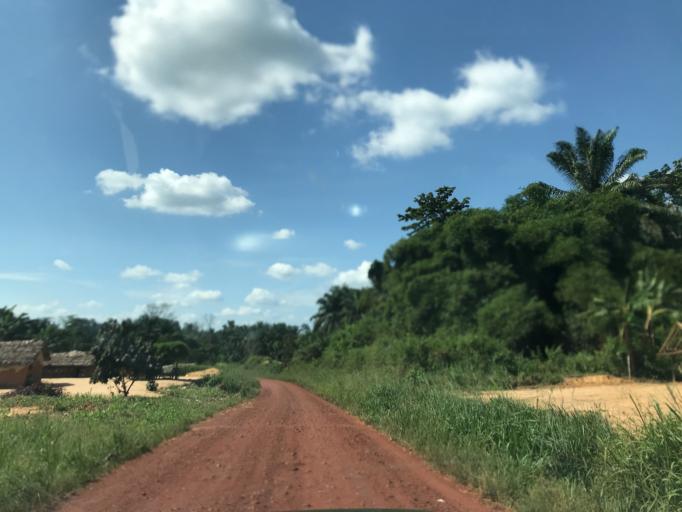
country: CD
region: Eastern Province
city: Kisangani
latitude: 1.2206
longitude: 25.2684
